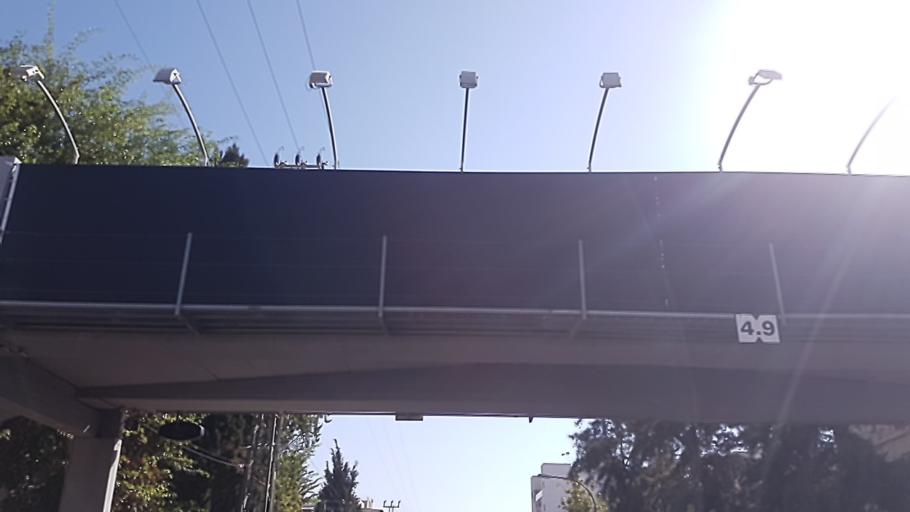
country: IL
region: Tel Aviv
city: Giv`atayim
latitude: 32.0667
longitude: 34.8241
